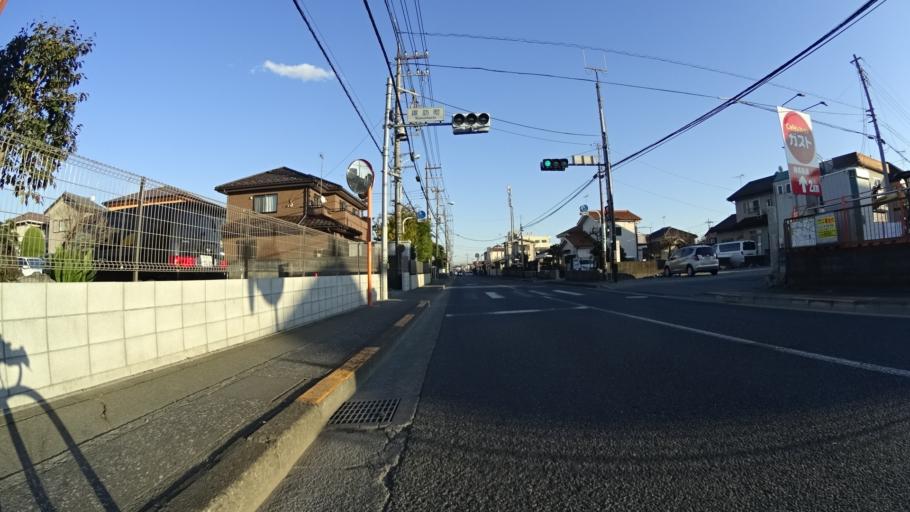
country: JP
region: Tokyo
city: Hachioji
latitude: 35.6756
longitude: 139.2902
